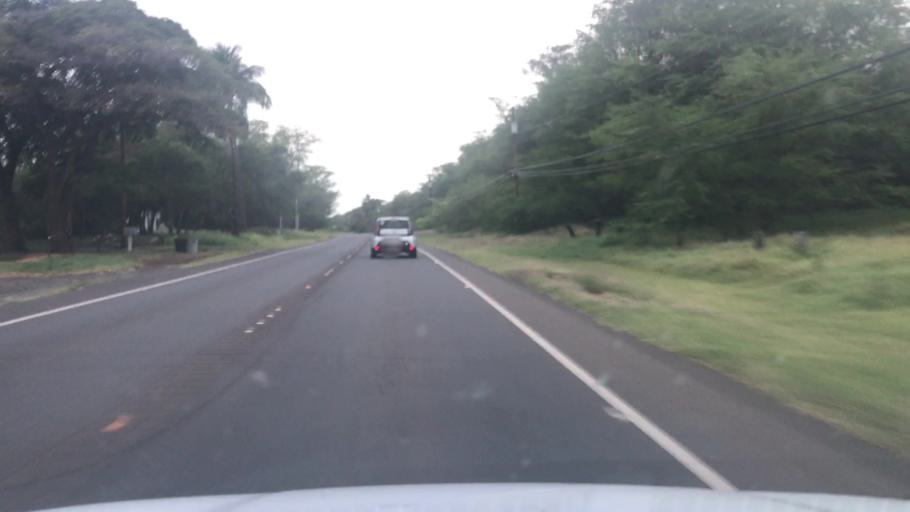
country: US
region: Hawaii
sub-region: Maui County
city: Kaunakakai
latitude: 21.0681
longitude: -156.9594
